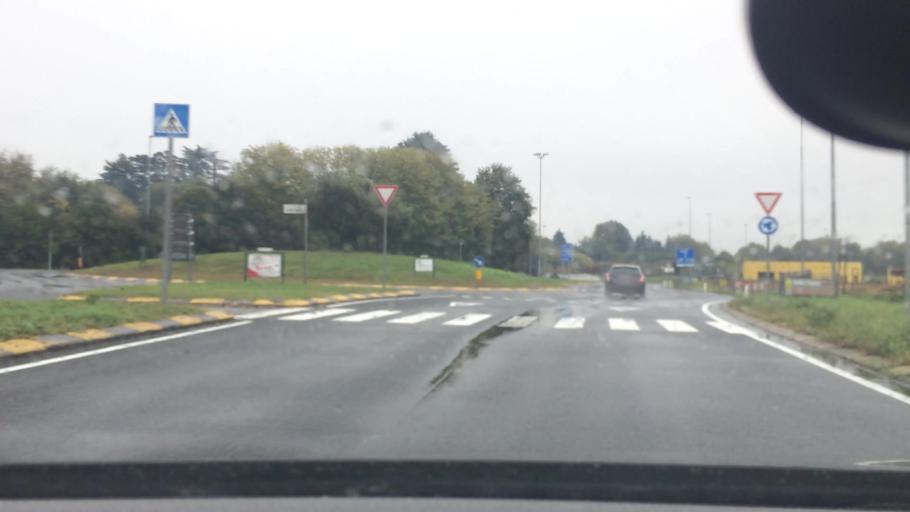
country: IT
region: Lombardy
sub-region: Provincia di Como
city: Lomazzo
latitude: 45.6935
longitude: 9.0320
